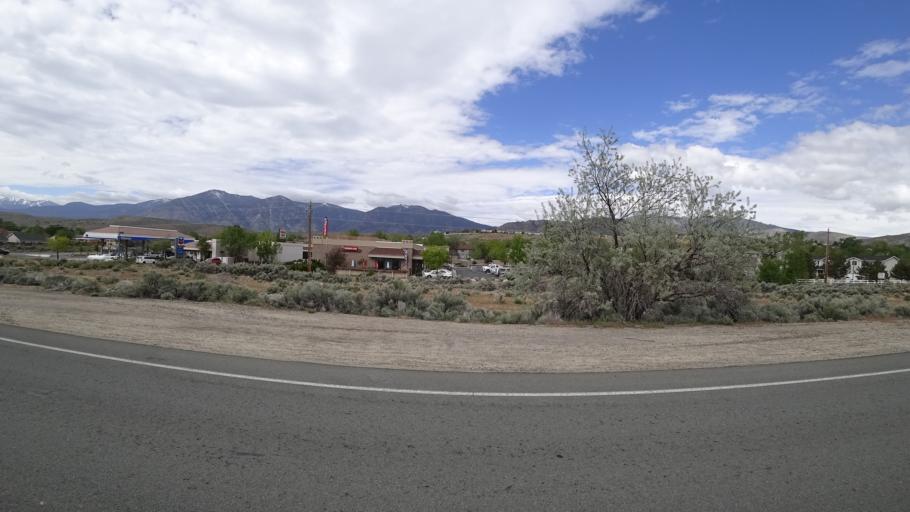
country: US
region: Nevada
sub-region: Douglas County
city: Indian Hills
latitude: 39.0923
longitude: -119.7752
